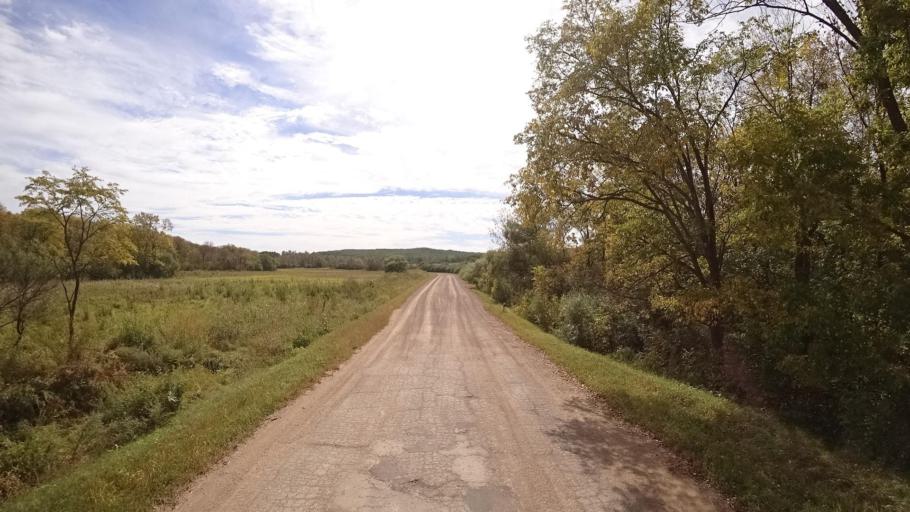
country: RU
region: Primorskiy
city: Yakovlevka
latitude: 44.6204
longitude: 133.5974
